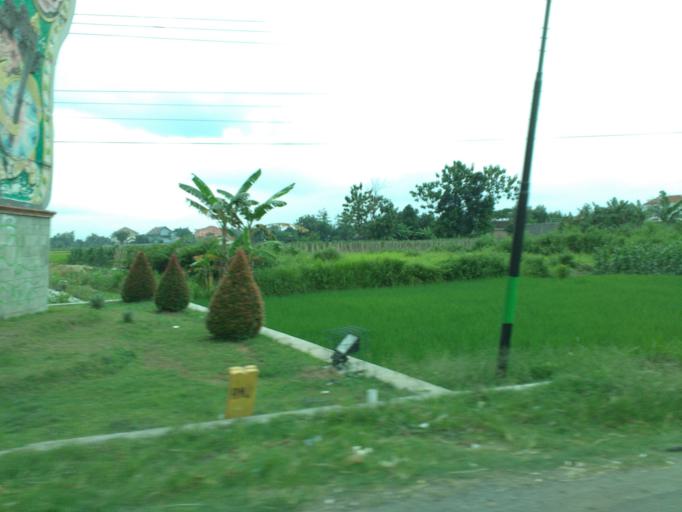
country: ID
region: Central Java
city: Gatak
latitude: -7.5924
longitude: 110.7027
